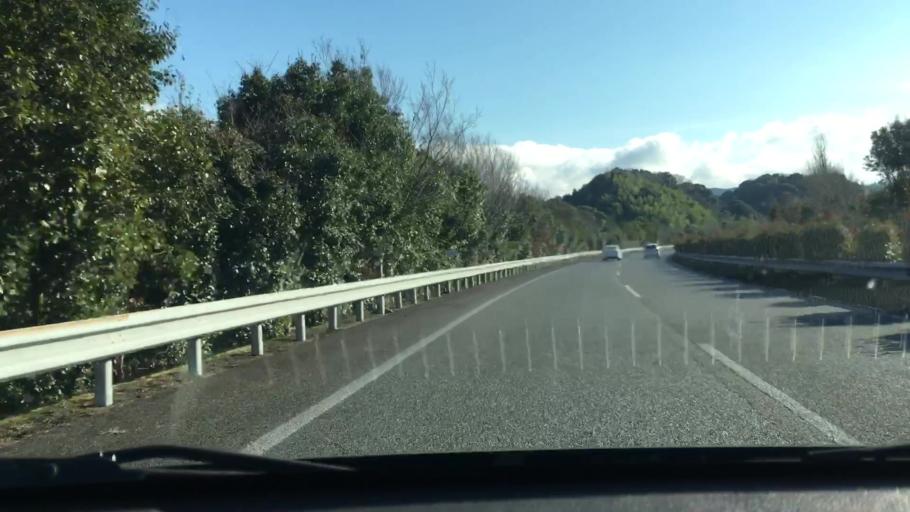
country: JP
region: Kumamoto
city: Hitoyoshi
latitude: 32.1967
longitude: 130.7776
